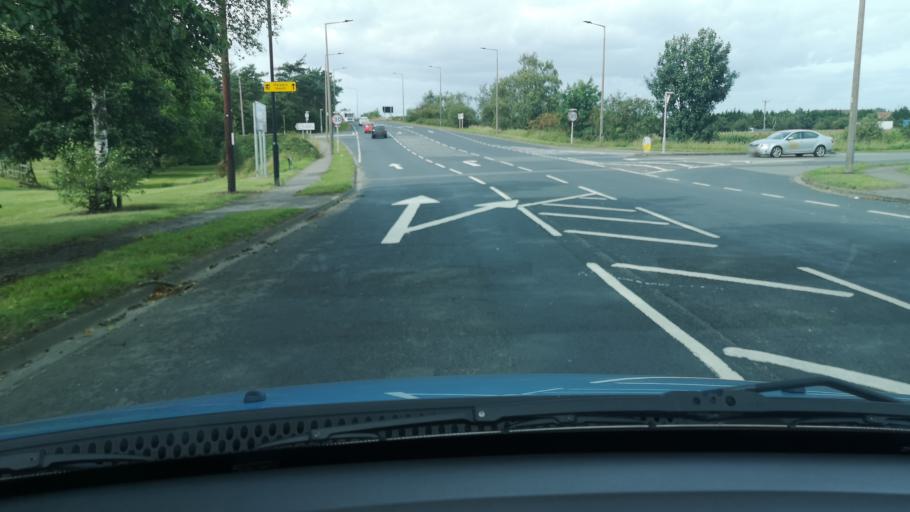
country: GB
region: England
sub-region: Doncaster
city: Hatfield
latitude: 53.5769
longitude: -0.9866
